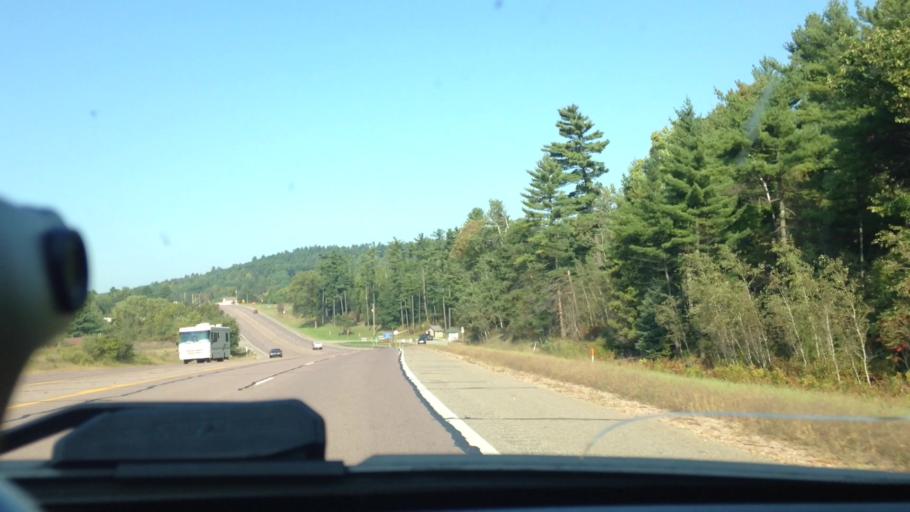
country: US
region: Michigan
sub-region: Dickinson County
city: Quinnesec
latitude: 45.8050
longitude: -87.9755
